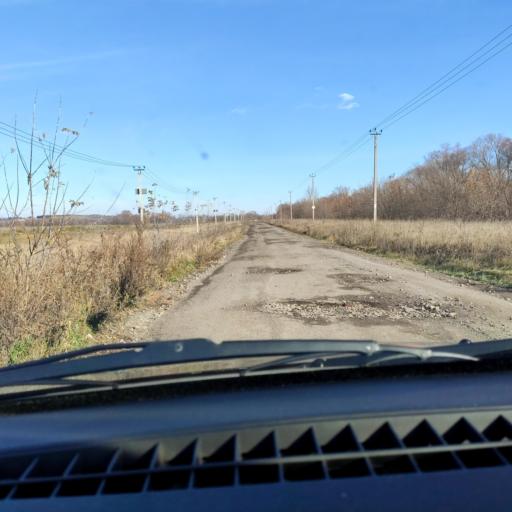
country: RU
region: Bashkortostan
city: Avdon
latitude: 54.4976
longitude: 55.8678
